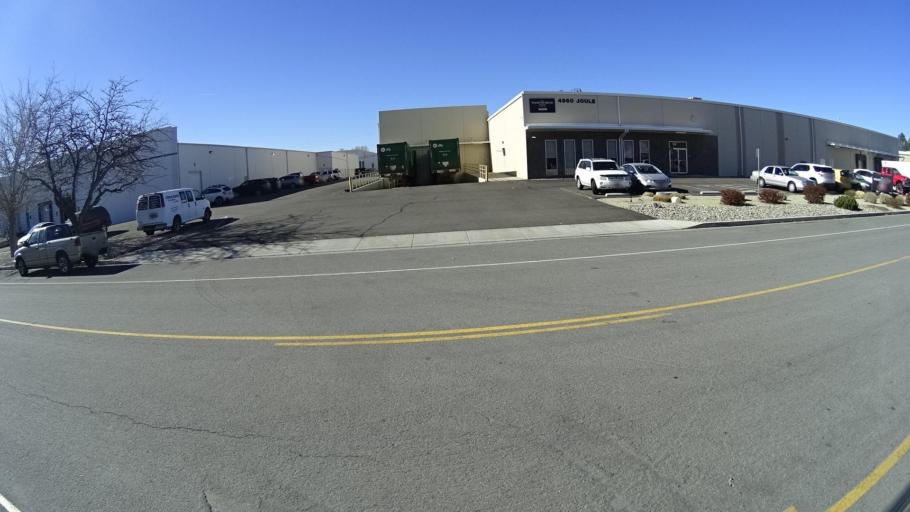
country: US
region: Nevada
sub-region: Washoe County
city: Sparks
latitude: 39.5081
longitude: -119.7583
